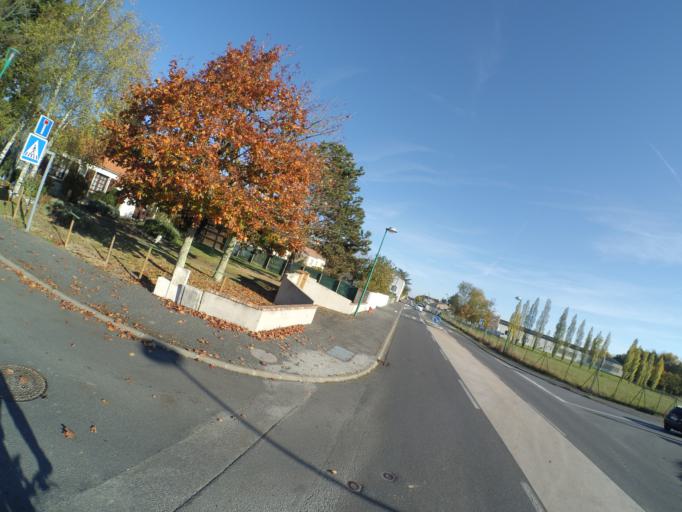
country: FR
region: Pays de la Loire
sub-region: Departement de la Loire-Atlantique
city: Saint-Lumine-de-Clisson
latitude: 47.0838
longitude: -1.3413
